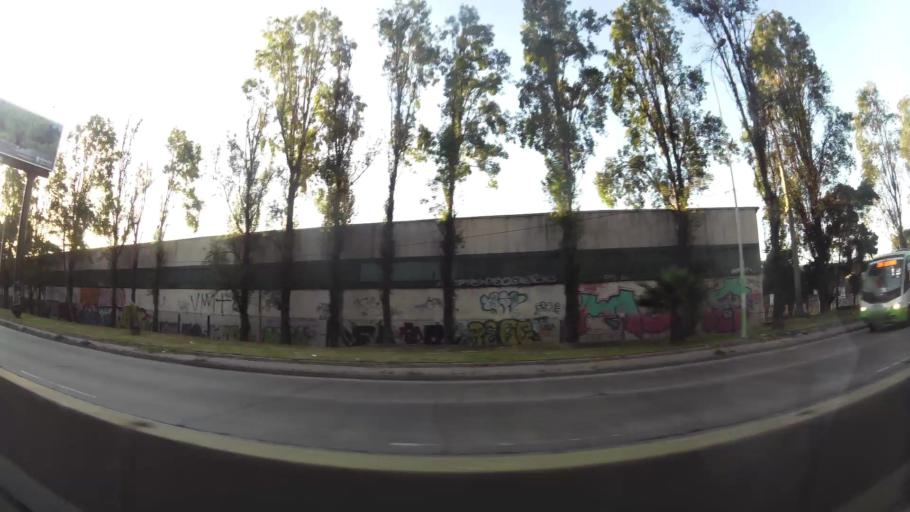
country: CL
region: Valparaiso
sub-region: Provincia de Valparaiso
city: Valparaiso
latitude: -33.0390
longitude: -71.6029
